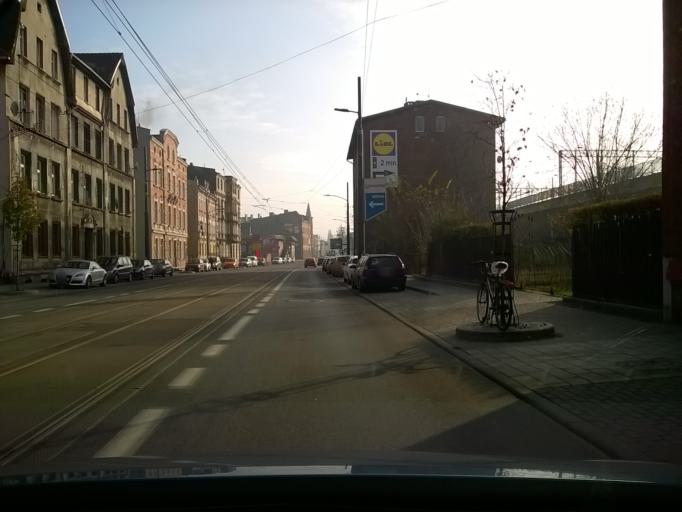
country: PL
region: Silesian Voivodeship
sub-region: Swietochlowice
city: Swietochlowice
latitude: 50.2808
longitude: 18.9412
